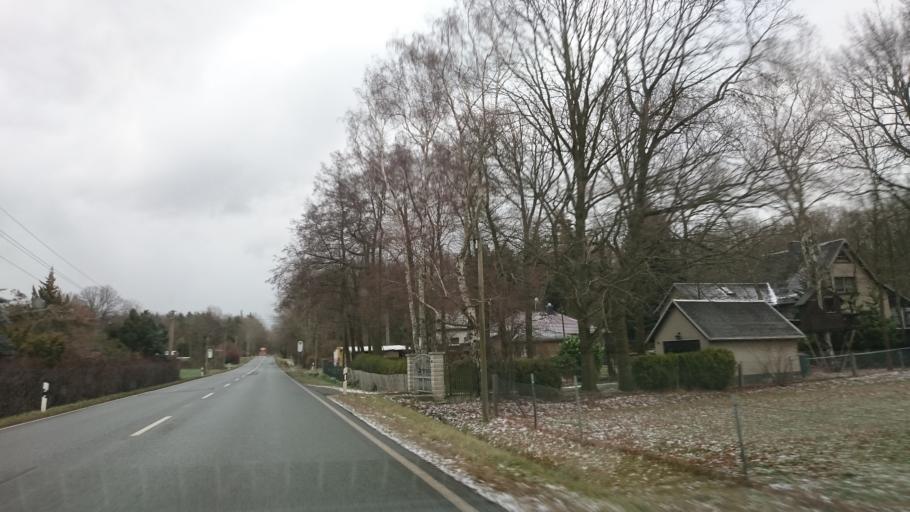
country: DE
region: Saxony
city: Hartmannsdorf
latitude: 50.7310
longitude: 12.4175
